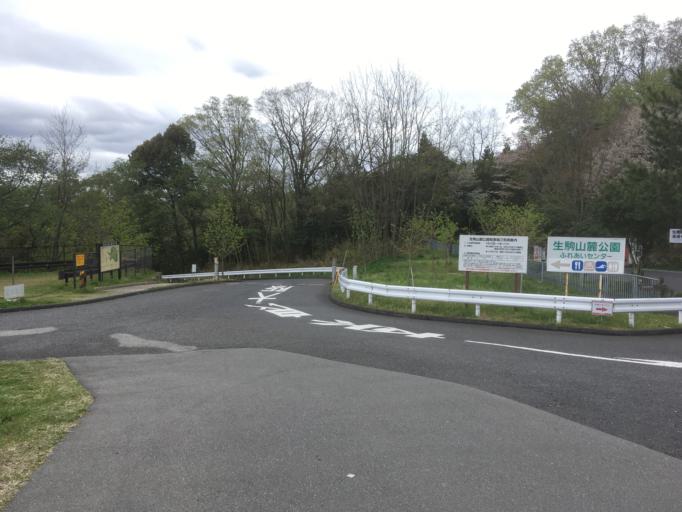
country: JP
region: Nara
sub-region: Ikoma-shi
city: Ikoma
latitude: 34.6993
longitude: 135.6743
